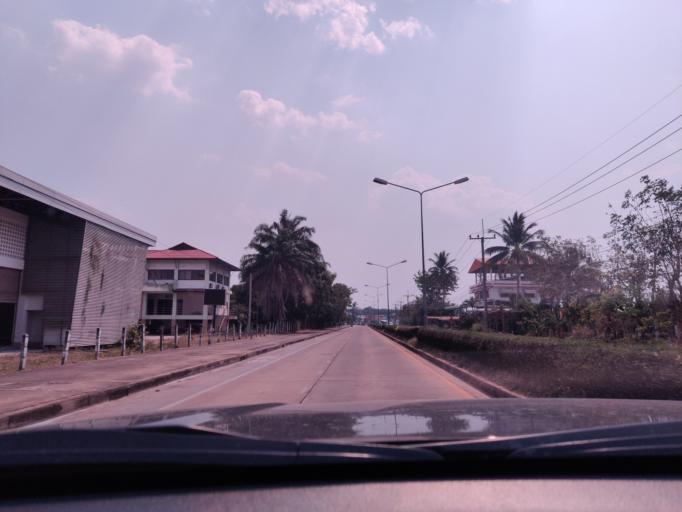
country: TH
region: Sisaket
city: Si Sa Ket
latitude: 15.1030
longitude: 104.3150
